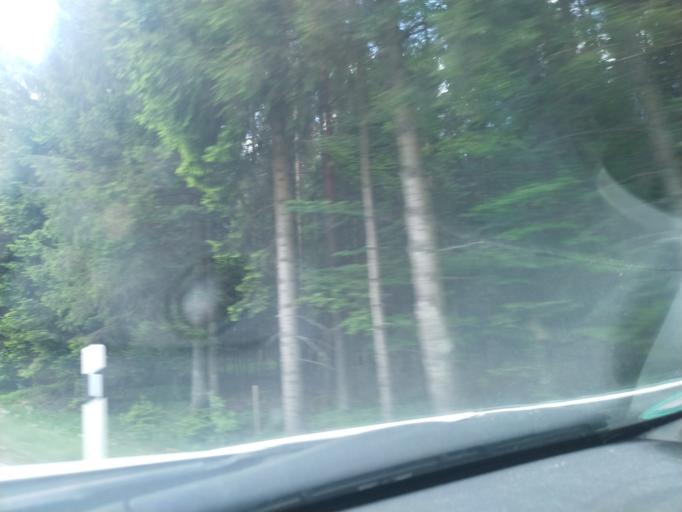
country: DE
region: Baden-Wuerttemberg
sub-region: Karlsruhe Region
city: Baiersbronn
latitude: 48.5833
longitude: 8.4201
